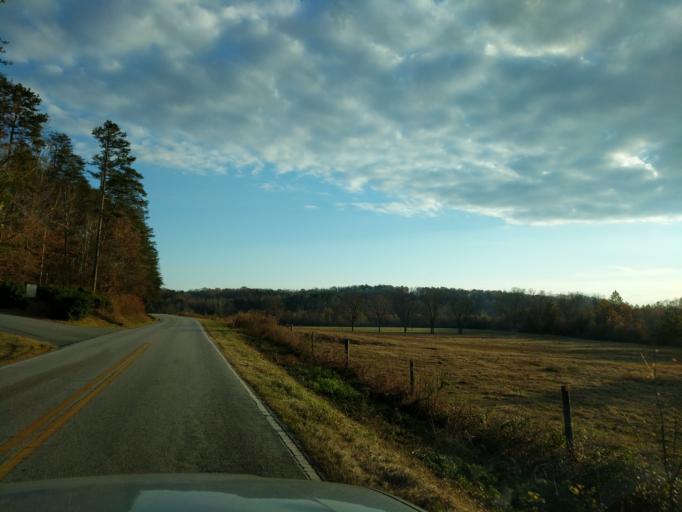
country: US
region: North Carolina
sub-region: Rutherford County
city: Rutherfordton
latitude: 35.3012
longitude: -81.9866
